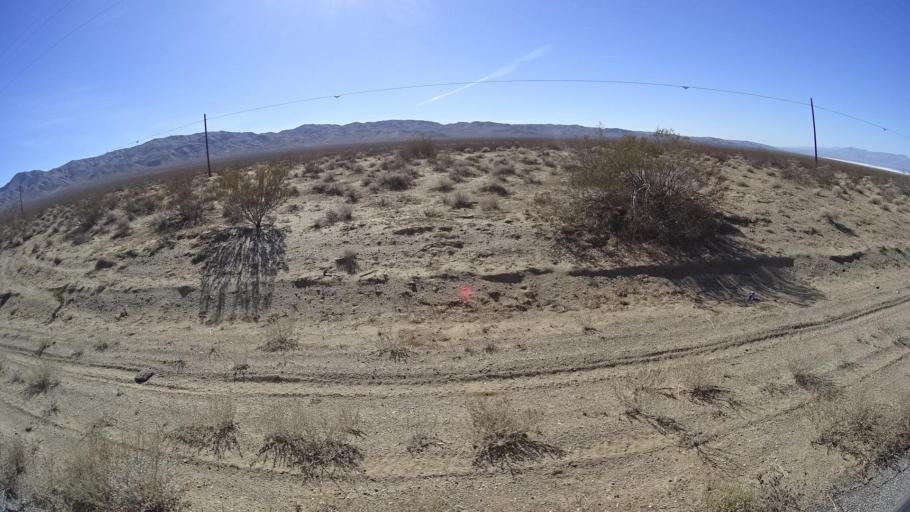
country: US
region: California
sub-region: Kern County
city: Ridgecrest
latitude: 35.3851
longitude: -117.7245
